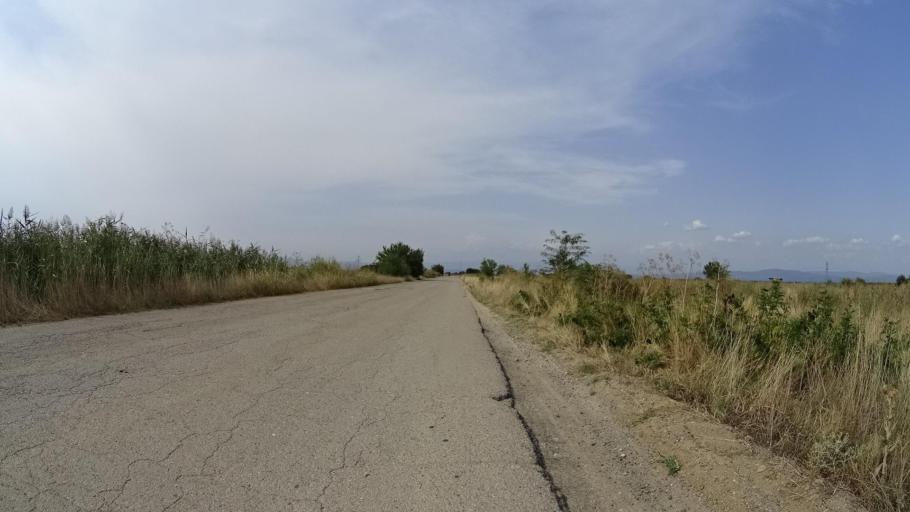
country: BG
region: Plovdiv
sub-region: Obshtina Kaloyanovo
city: Kaloyanovo
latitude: 42.3149
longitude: 24.7996
